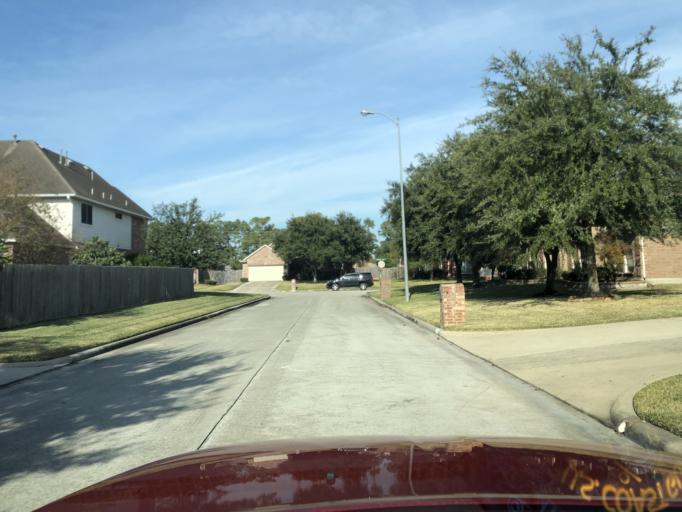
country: US
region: Texas
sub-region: Harris County
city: Tomball
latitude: 30.0277
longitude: -95.5576
